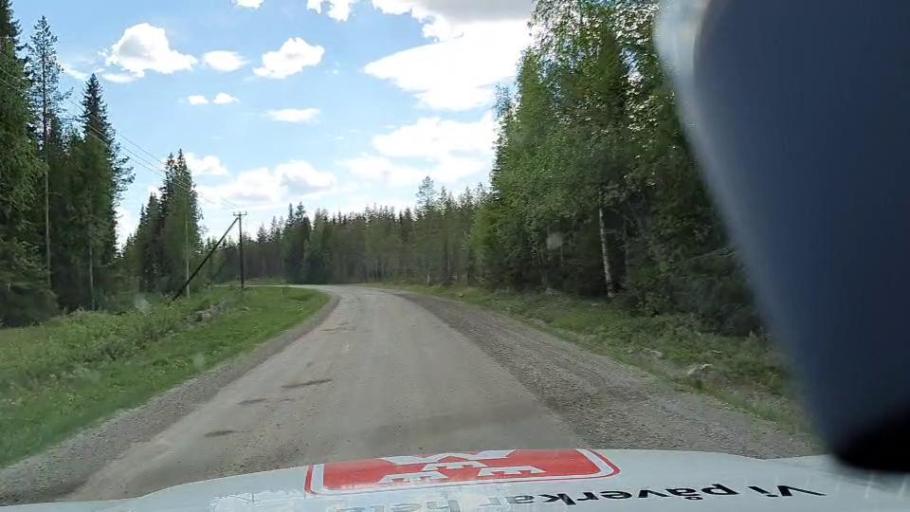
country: SE
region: Jaemtland
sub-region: Stroemsunds Kommun
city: Stroemsund
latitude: 64.5318
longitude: 15.5934
